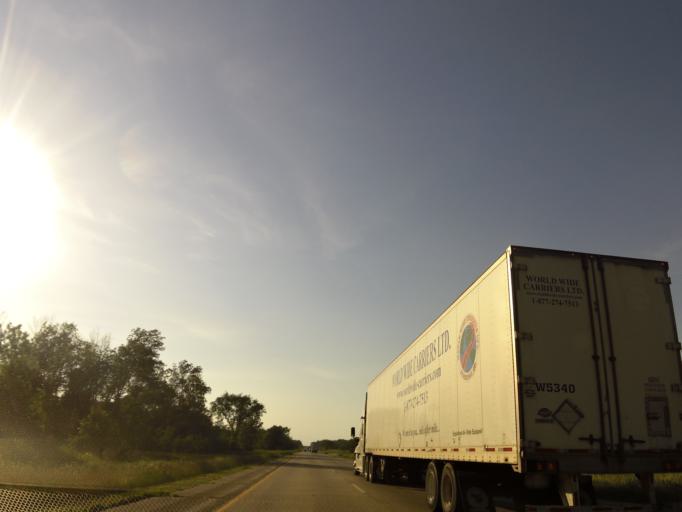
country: US
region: Wisconsin
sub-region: Juneau County
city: Mauston
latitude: 43.8526
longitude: -90.1060
